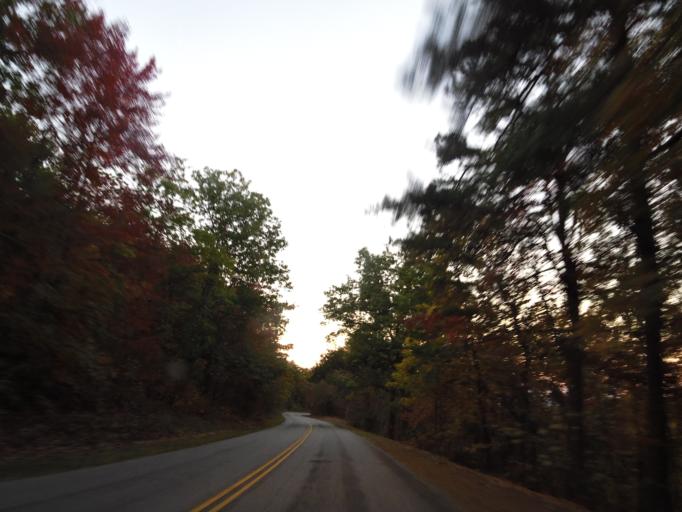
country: US
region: Tennessee
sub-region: Blount County
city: Maryville
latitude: 35.6629
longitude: -83.9109
